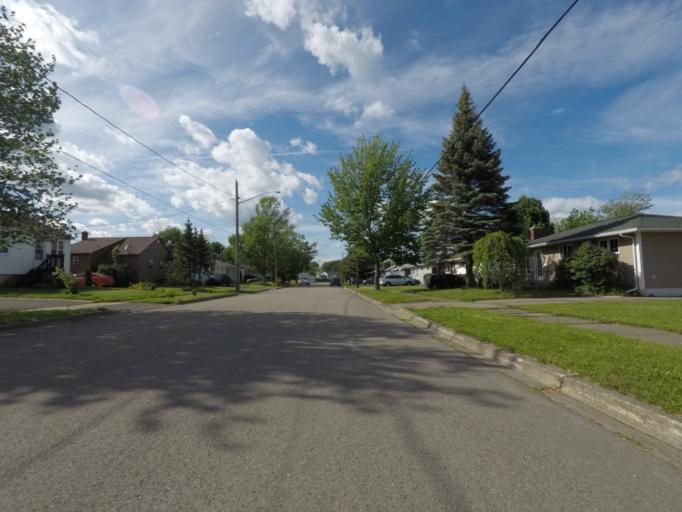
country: CA
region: New Brunswick
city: Moncton
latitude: 46.1025
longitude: -64.8242
